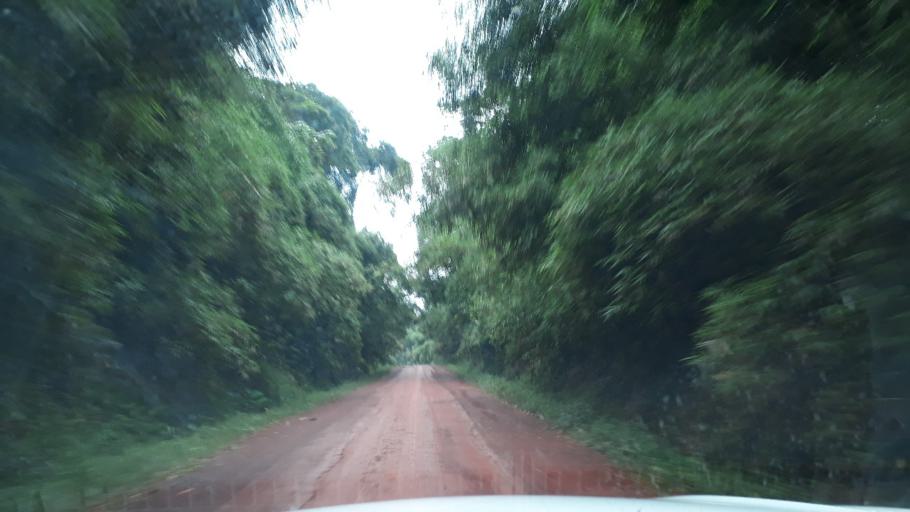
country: CD
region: Eastern Province
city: Wamba
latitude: 1.3478
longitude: 27.5874
